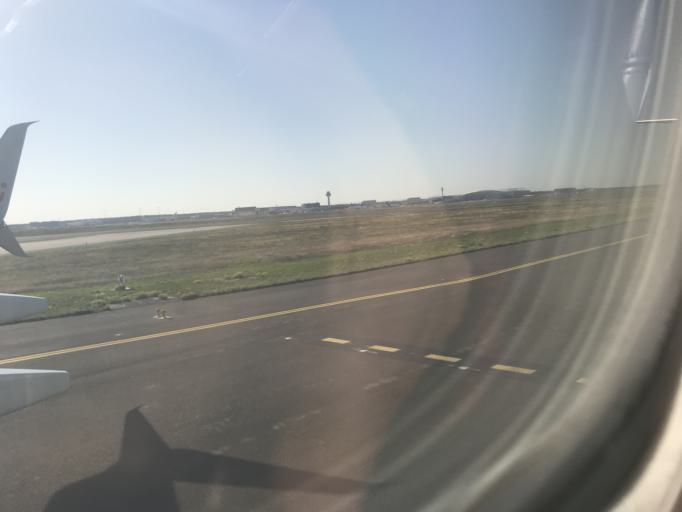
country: DE
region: Hesse
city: Kelsterbach
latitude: 50.0436
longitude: 8.5726
